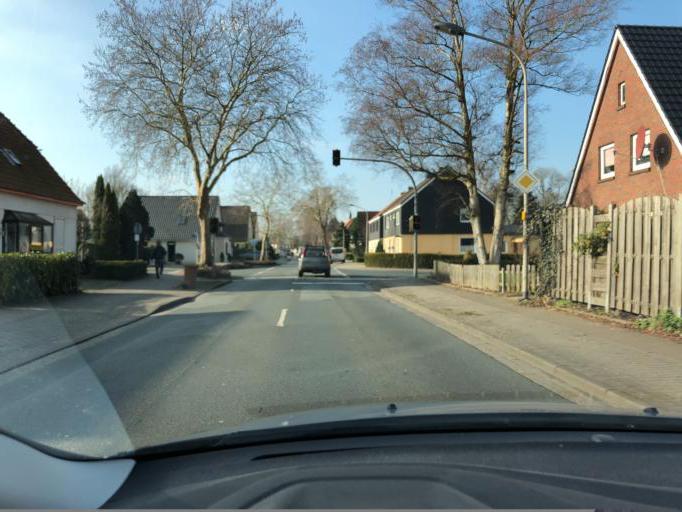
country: DE
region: Lower Saxony
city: Westerstede
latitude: 53.2600
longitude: 7.9264
